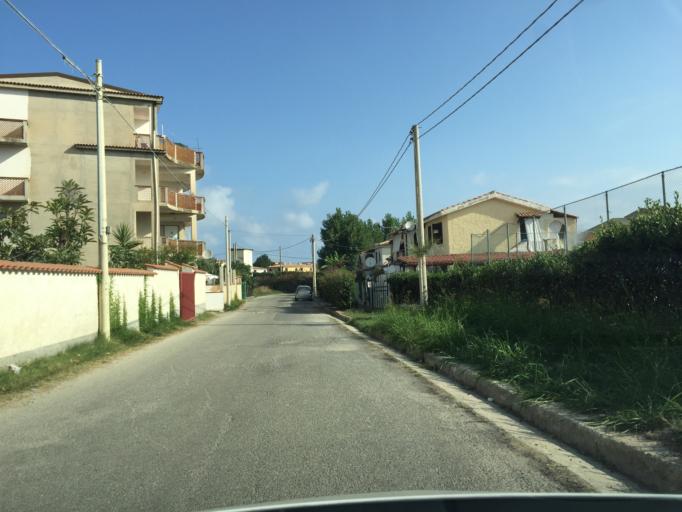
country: IT
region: Calabria
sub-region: Provincia di Vibo-Valentia
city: Briatico
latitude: 38.7198
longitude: 16.0548
